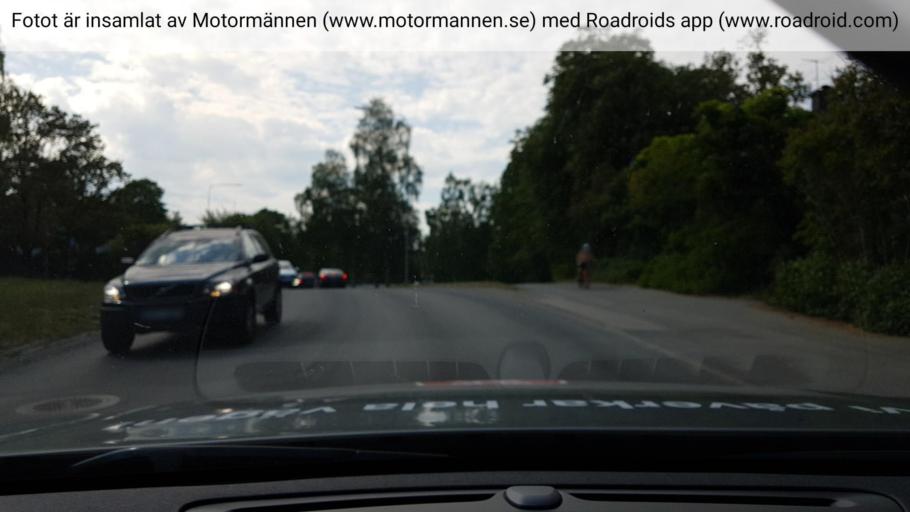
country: SE
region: Stockholm
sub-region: Lidingo
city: Lidingoe
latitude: 59.3628
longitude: 18.1498
